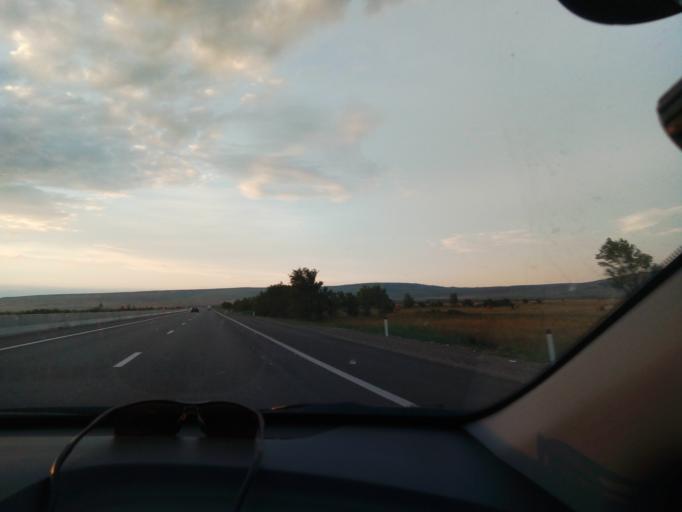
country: RU
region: Stavropol'skiy
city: Barsukovskaya
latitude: 44.7650
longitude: 41.8606
